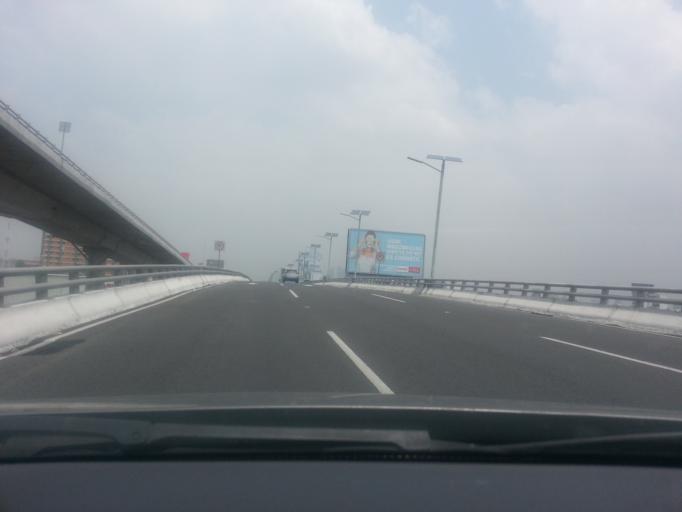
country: MX
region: Mexico City
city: Colonia del Valle
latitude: 19.3863
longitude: -99.1902
